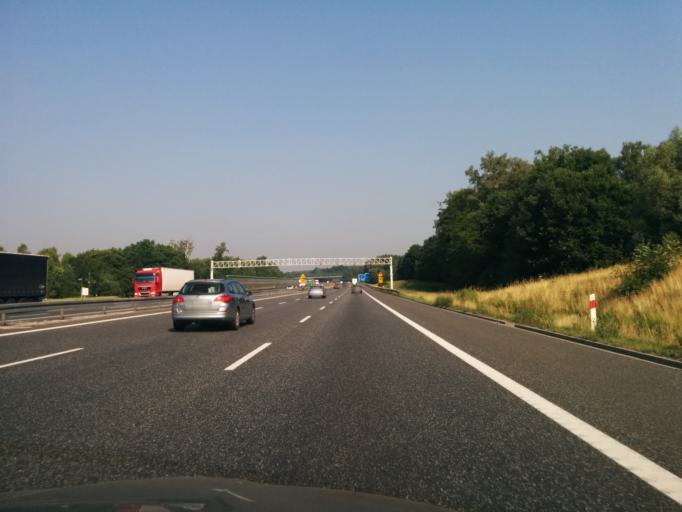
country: PL
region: Silesian Voivodeship
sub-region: Powiat gliwicki
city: Paniowki
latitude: 50.2650
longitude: 18.7807
